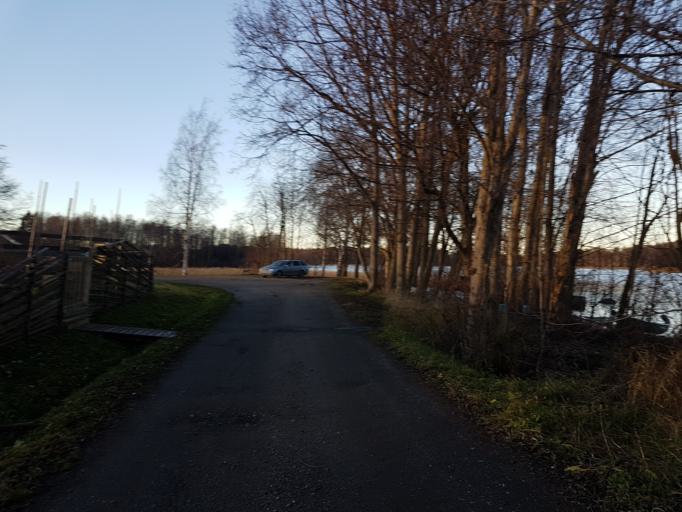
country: FI
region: Northern Savo
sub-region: Kuopio
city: Kuopio
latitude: 62.9300
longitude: 27.6251
